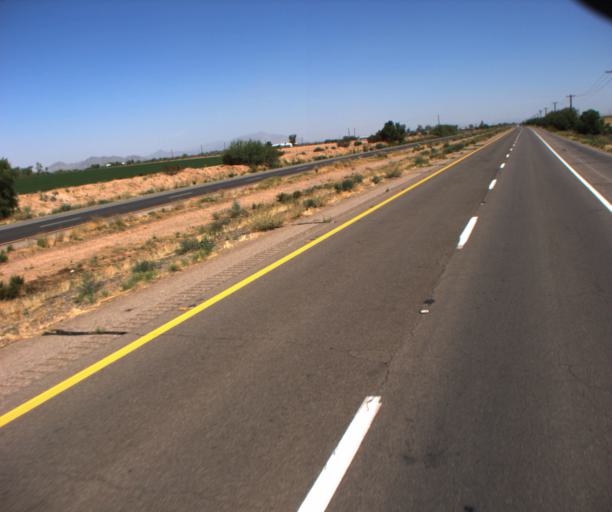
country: US
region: Arizona
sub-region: Pinal County
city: Maricopa
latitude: 32.8972
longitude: -112.0493
